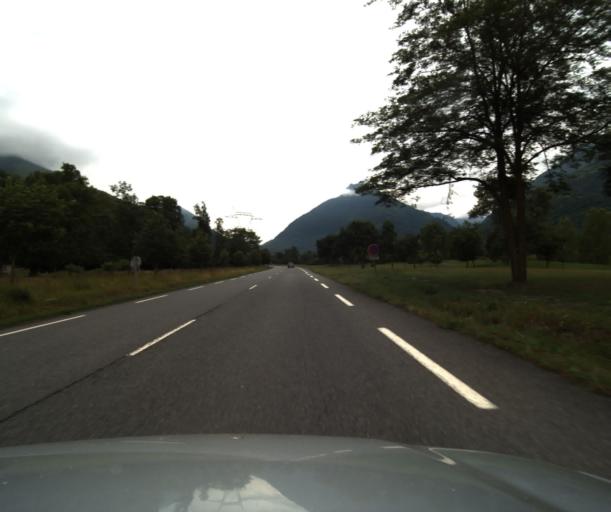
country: FR
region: Midi-Pyrenees
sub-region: Departement des Hautes-Pyrenees
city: Pierrefitte-Nestalas
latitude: 42.9857
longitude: -0.0721
